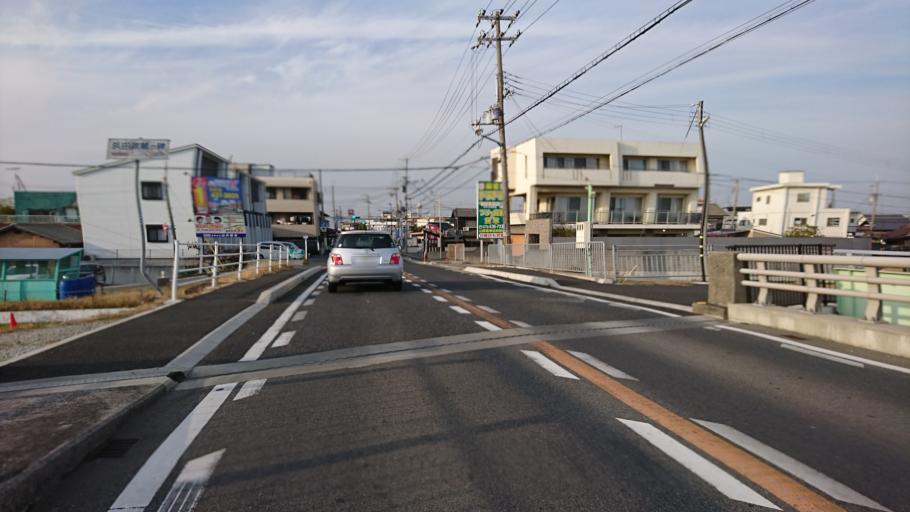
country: JP
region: Hyogo
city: Kakogawacho-honmachi
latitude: 34.7148
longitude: 134.8616
